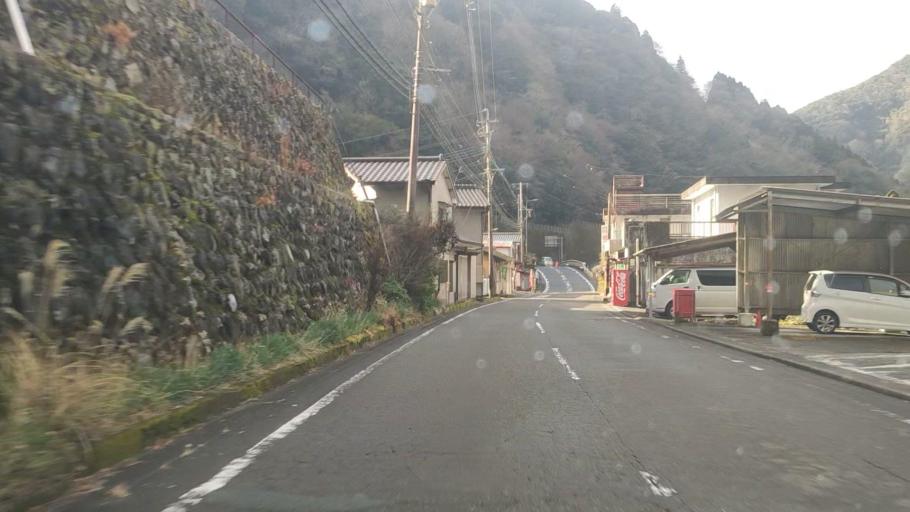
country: JP
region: Kumamoto
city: Hitoyoshi
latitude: 32.4194
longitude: 130.8537
